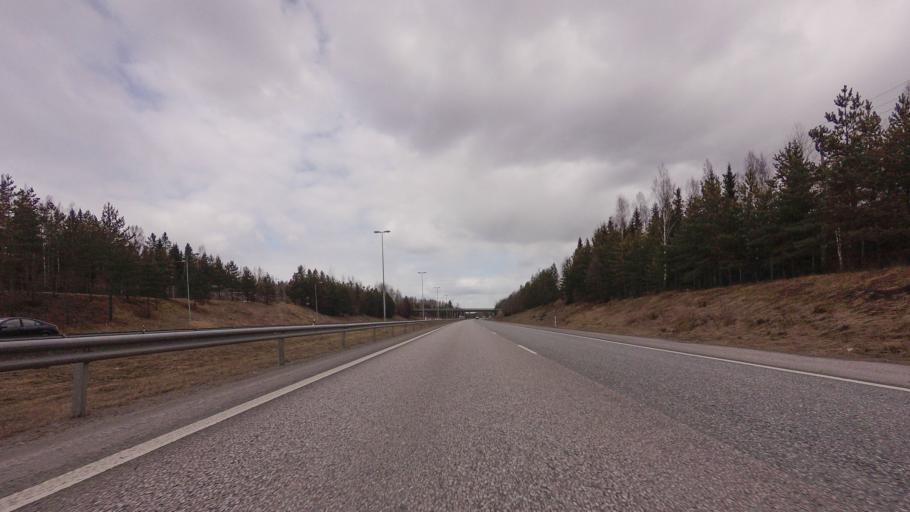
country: FI
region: Uusimaa
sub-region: Helsinki
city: Nurmijaervi
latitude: 60.3585
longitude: 24.8085
